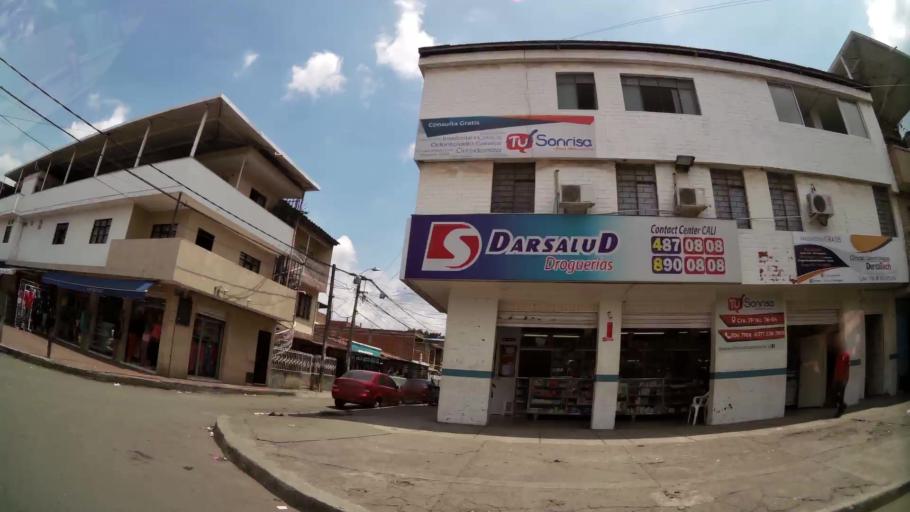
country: CO
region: Valle del Cauca
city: Cali
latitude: 3.4555
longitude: -76.4803
